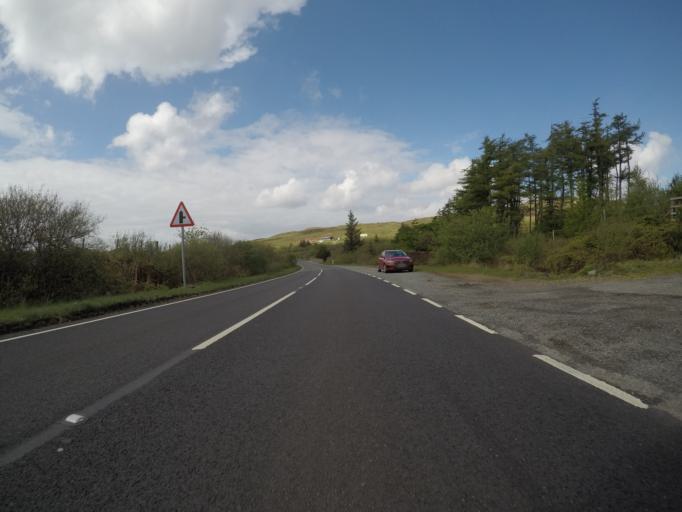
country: GB
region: Scotland
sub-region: Highland
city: Portree
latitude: 57.5300
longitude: -6.3493
